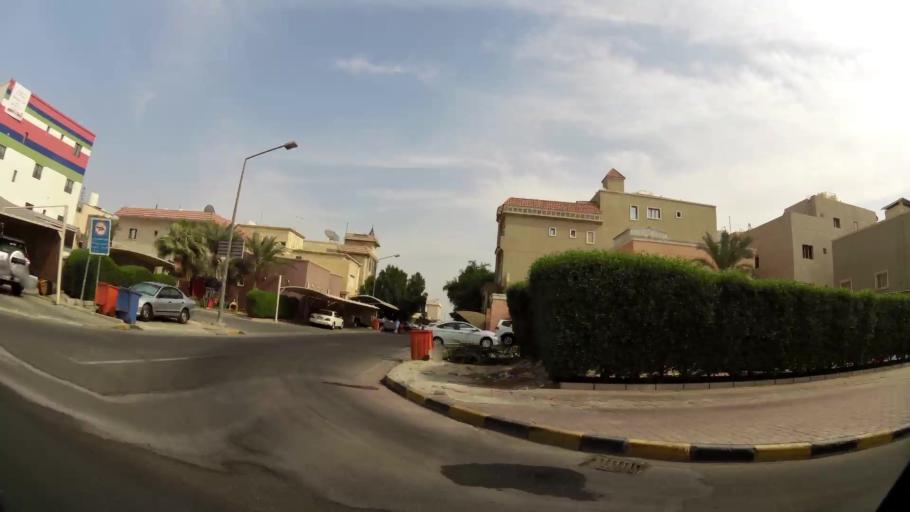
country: KW
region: Al Asimah
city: Ash Shamiyah
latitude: 29.3337
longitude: 47.9620
